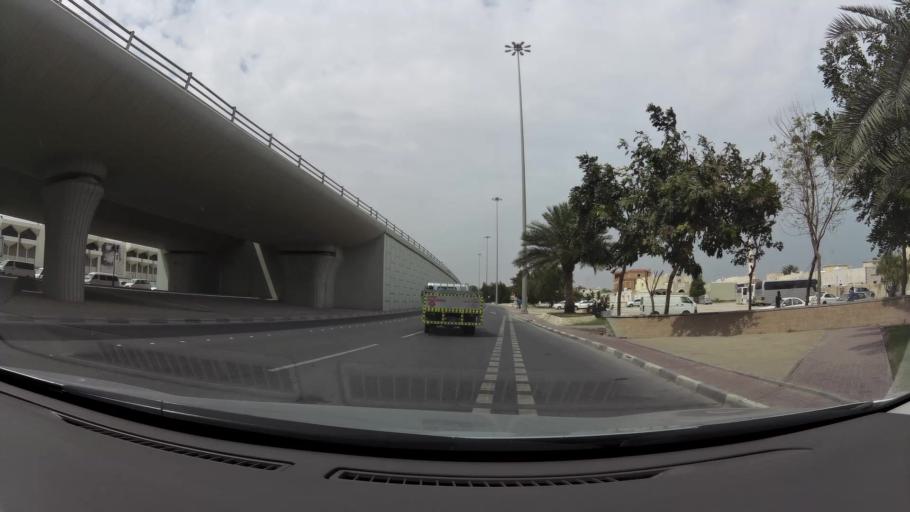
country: QA
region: Baladiyat ar Rayyan
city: Ar Rayyan
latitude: 25.3213
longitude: 51.4699
